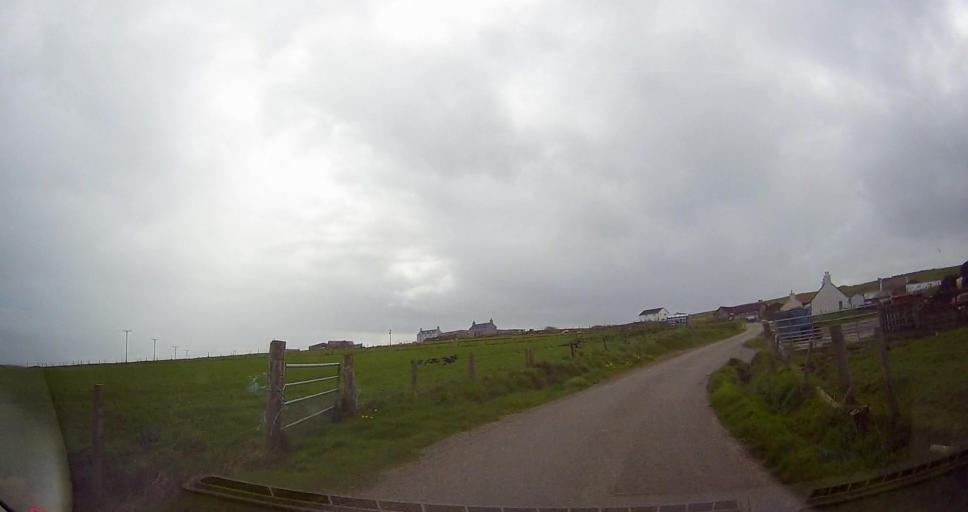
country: GB
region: Scotland
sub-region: Shetland Islands
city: Sandwick
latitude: 59.9110
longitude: -1.3317
